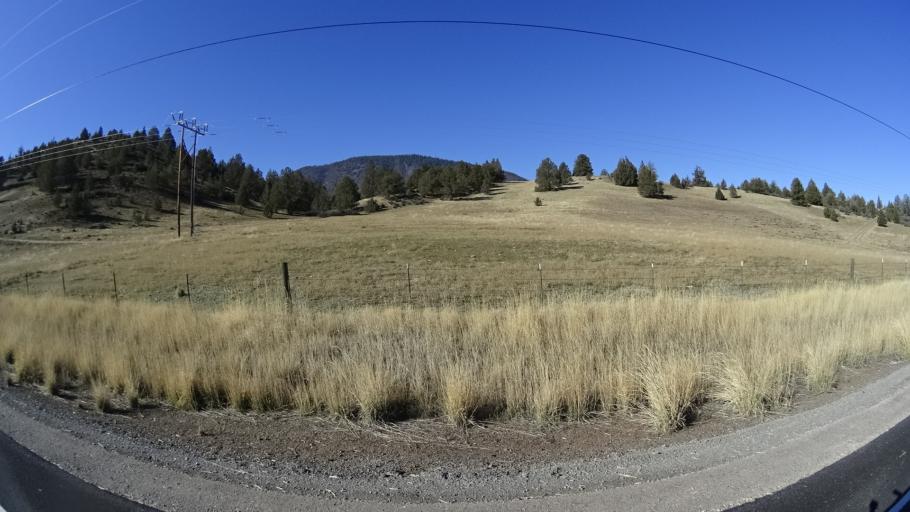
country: US
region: California
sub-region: Siskiyou County
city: Montague
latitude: 41.8636
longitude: -122.4640
